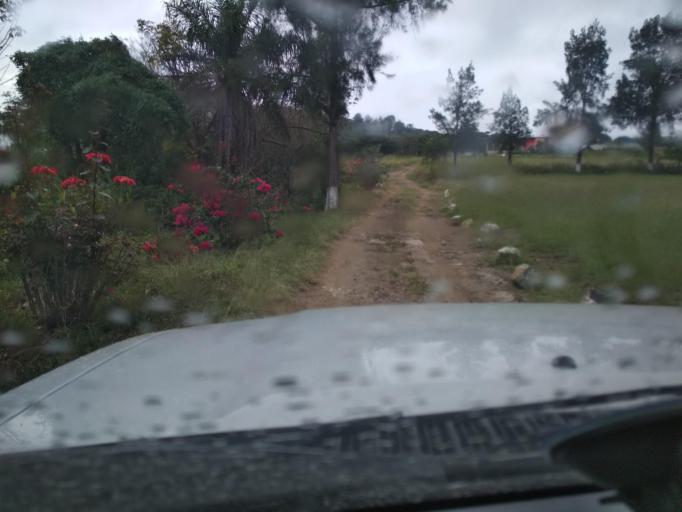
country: MX
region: Veracruz
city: El Castillo
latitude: 19.5345
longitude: -96.8217
